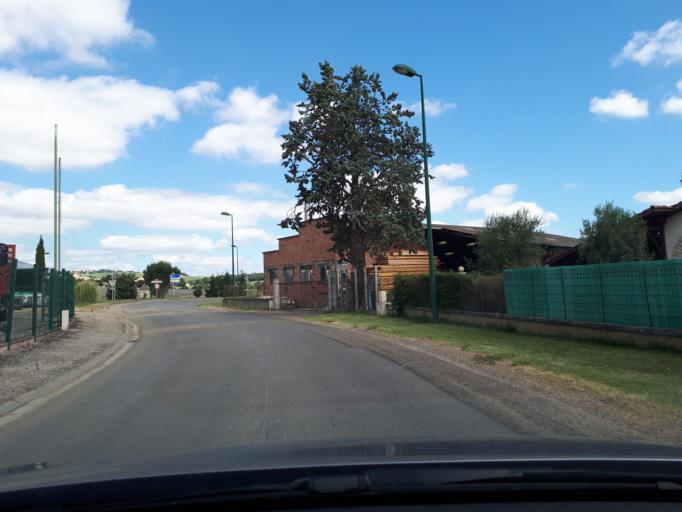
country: FR
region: Midi-Pyrenees
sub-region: Departement du Tarn-et-Garonne
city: Lavit
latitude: 43.9971
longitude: 0.8195
